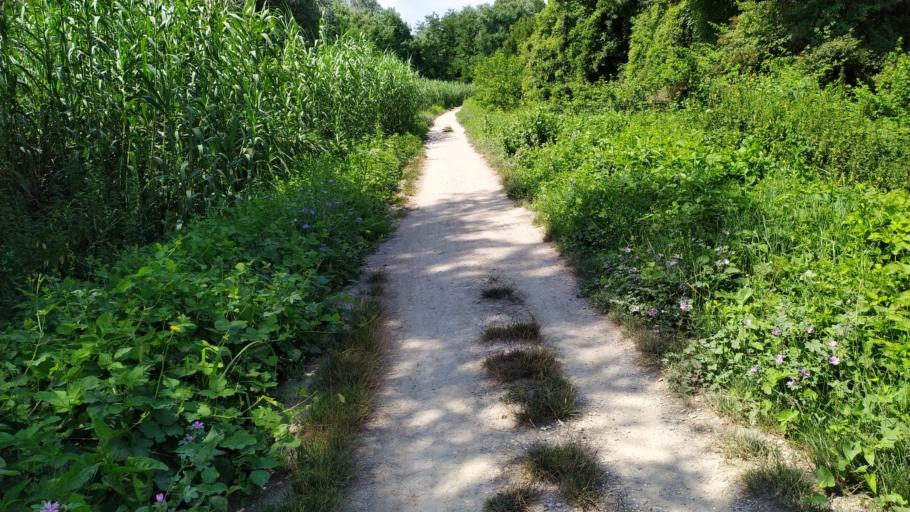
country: IT
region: Emilia-Romagna
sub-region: Forli-Cesena
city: Forli
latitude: 44.2113
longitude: 12.0243
